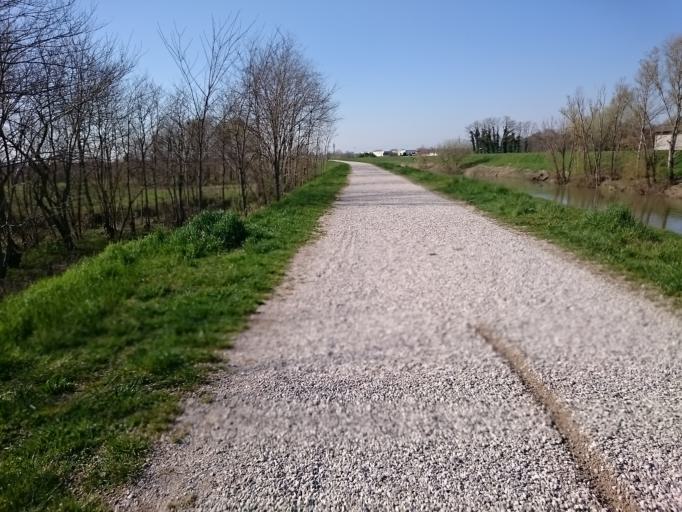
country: IT
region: Veneto
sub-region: Provincia di Padova
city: Ponte San Nicolo
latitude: 45.3743
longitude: 11.9307
